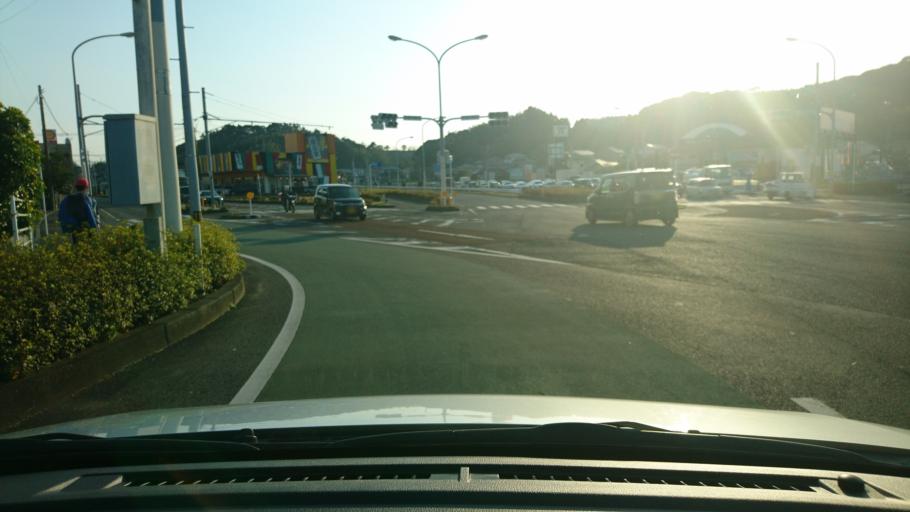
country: JP
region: Miyazaki
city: Miyazaki-shi
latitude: 31.9740
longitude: 131.4401
